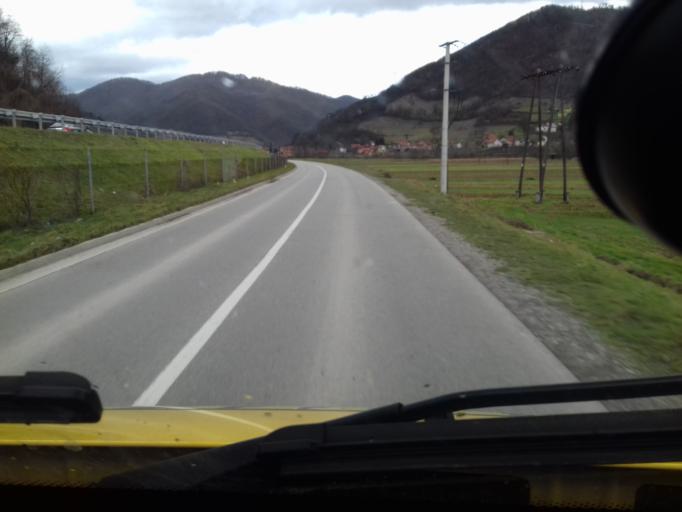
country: BA
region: Federation of Bosnia and Herzegovina
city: Dobrinje
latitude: 44.0439
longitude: 18.1198
